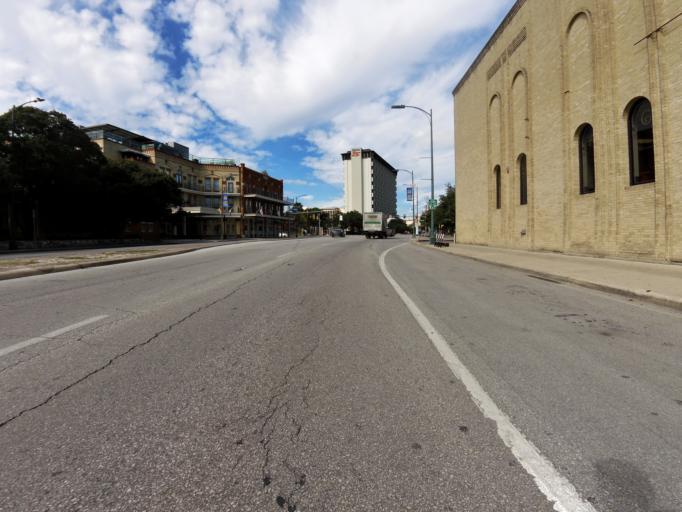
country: US
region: Texas
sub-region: Bexar County
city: San Antonio
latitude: 29.4199
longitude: -98.4882
